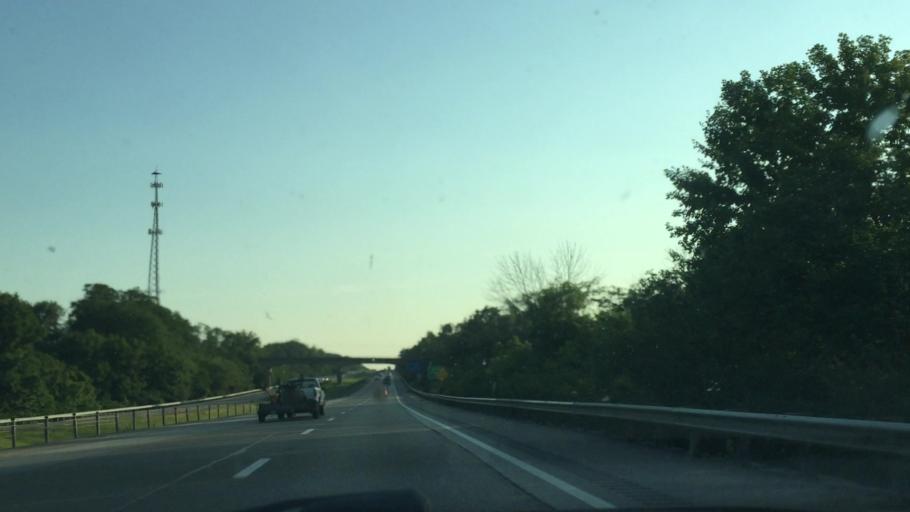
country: US
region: Kentucky
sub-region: Boone County
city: Walton
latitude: 38.8739
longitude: -84.6303
